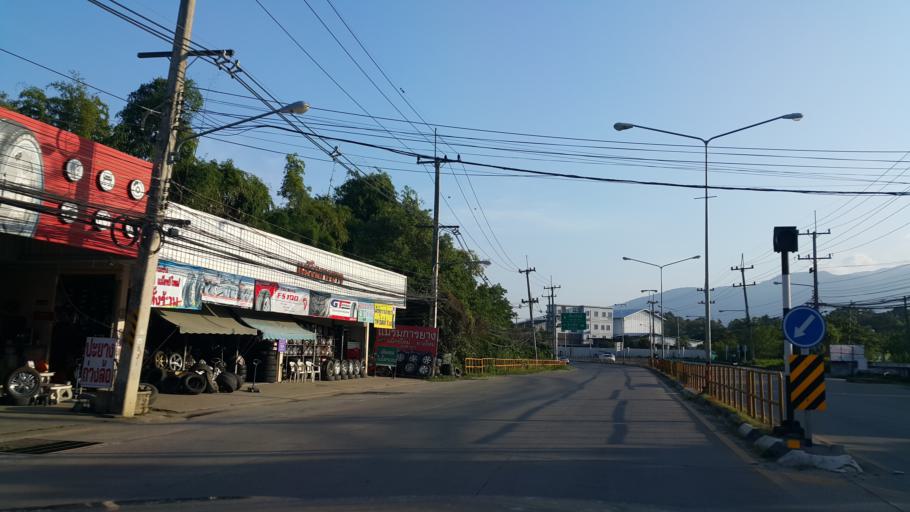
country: TH
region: Chiang Mai
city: San Sai
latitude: 18.9261
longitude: 98.9394
